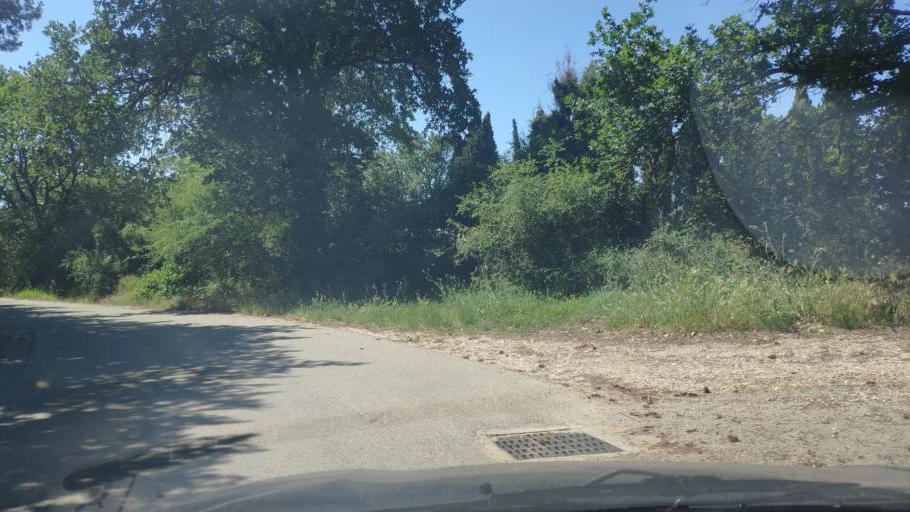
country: FR
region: Provence-Alpes-Cote d'Azur
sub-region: Departement du Vaucluse
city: Loriol-du-Comtat
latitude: 44.0750
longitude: 5.0123
